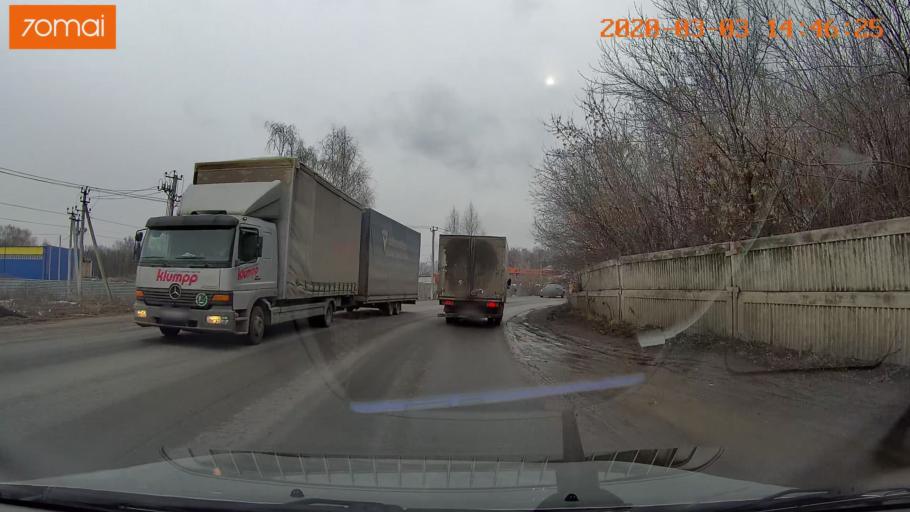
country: RU
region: Moskovskaya
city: Rodniki
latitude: 55.6974
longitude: 38.0582
